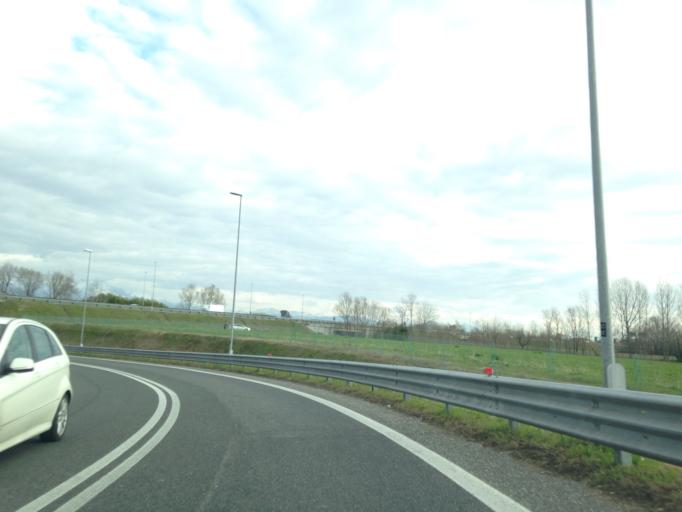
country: IT
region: Friuli Venezia Giulia
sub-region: Provincia di Pordenone
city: Porcia
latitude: 45.9425
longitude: 12.6224
